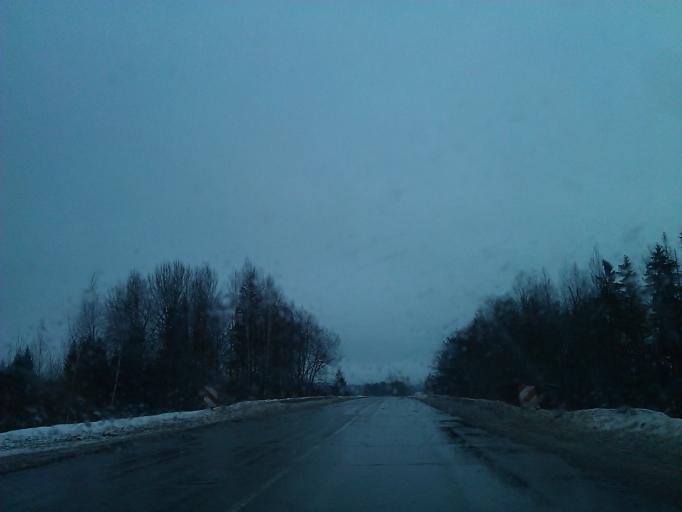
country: LV
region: Cesu Rajons
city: Cesis
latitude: 57.2829
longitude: 25.2928
